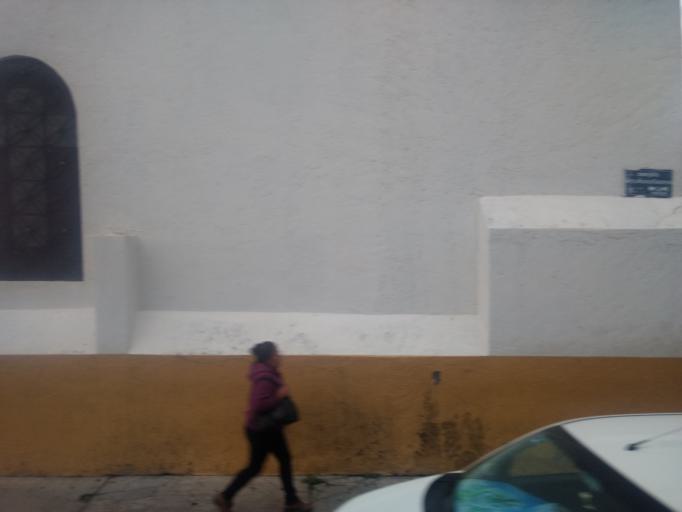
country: MX
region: Tlaxcala
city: Apizaco
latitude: 19.4173
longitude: -98.1456
